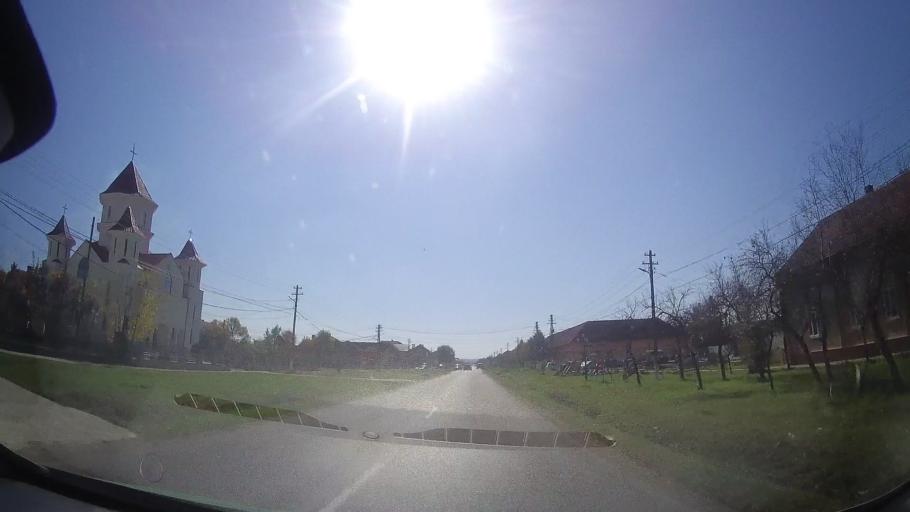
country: RO
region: Timis
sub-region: Comuna Bethausen
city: Bethausen
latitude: 45.8372
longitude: 21.9596
